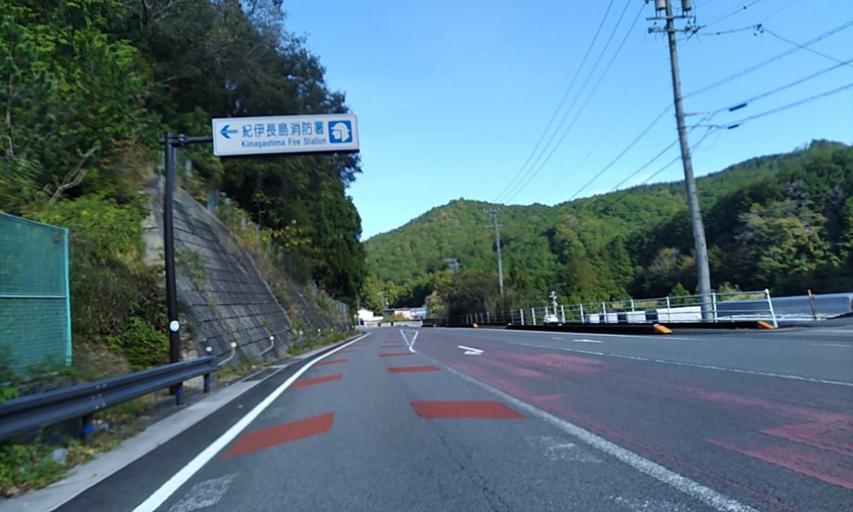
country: JP
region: Mie
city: Owase
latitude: 34.1926
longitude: 136.3113
